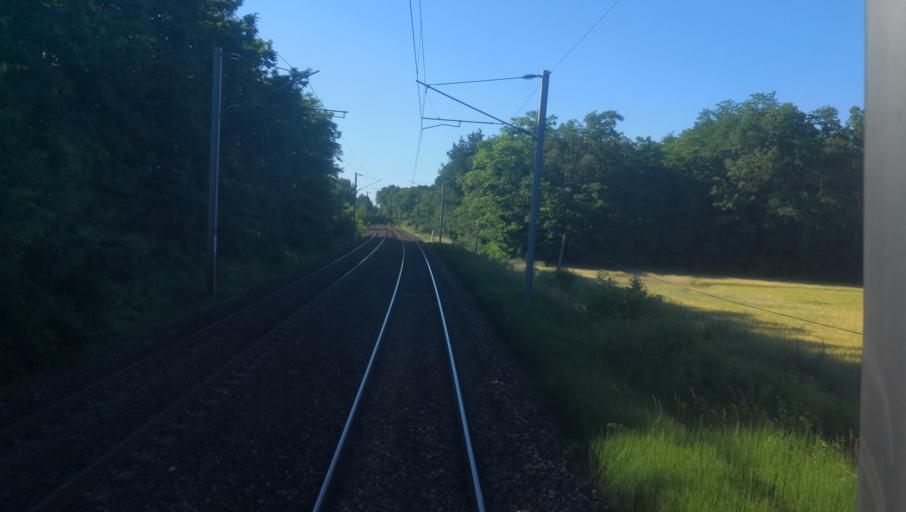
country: FR
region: Bourgogne
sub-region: Departement de la Nievre
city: La Charite-sur-Loire
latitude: 47.2244
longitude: 3.0162
